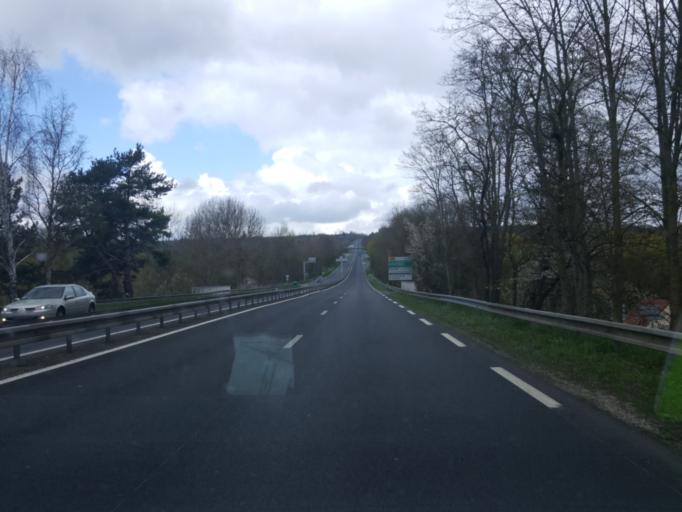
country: FR
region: Ile-de-France
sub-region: Departement du Val-d'Oise
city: Magny-en-Vexin
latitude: 49.1513
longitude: 1.7799
